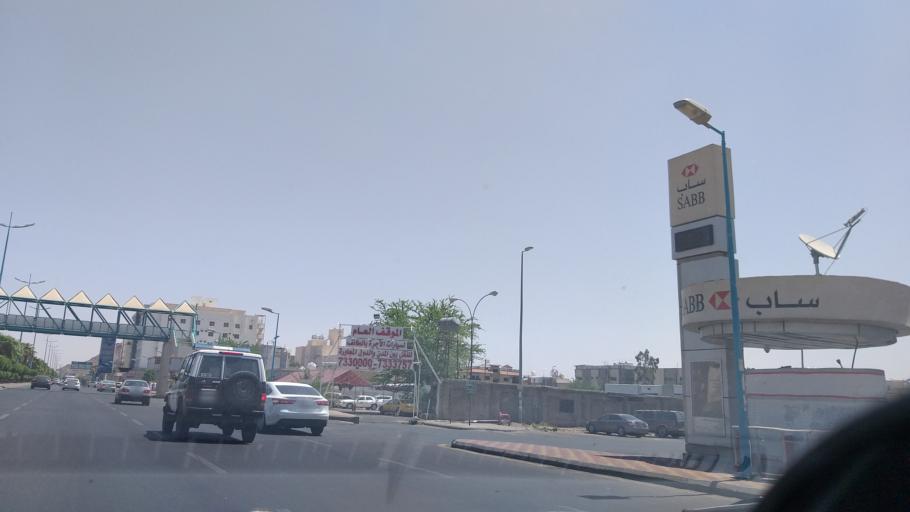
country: SA
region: Makkah
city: Ta'if
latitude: 21.2917
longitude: 40.4242
